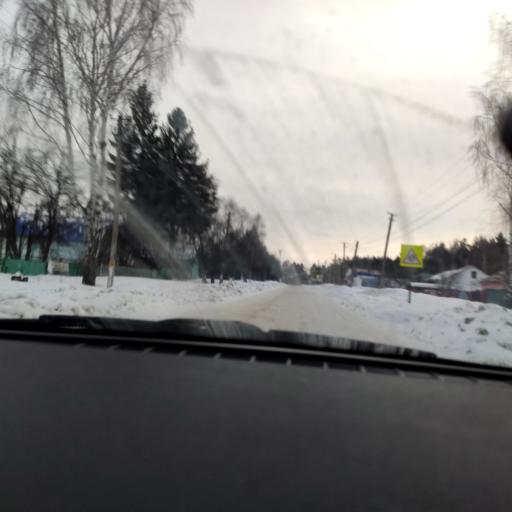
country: RU
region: Bashkortostan
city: Iglino
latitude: 54.7709
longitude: 56.5348
